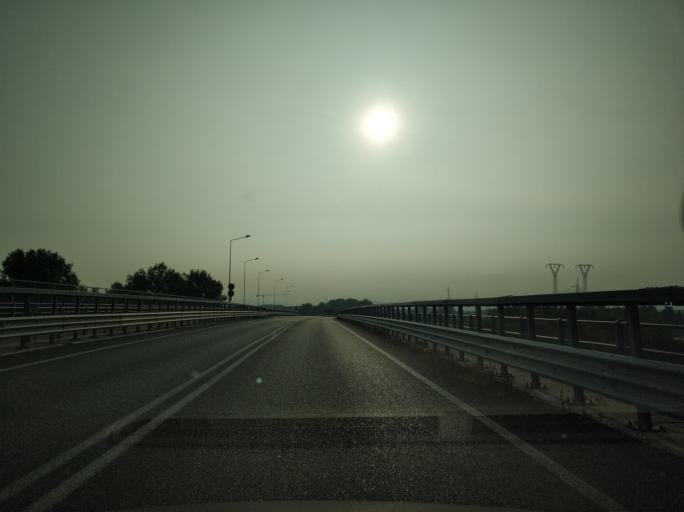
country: IT
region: Piedmont
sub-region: Provincia di Torino
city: Borgaro Torinese
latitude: 45.1486
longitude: 7.6417
